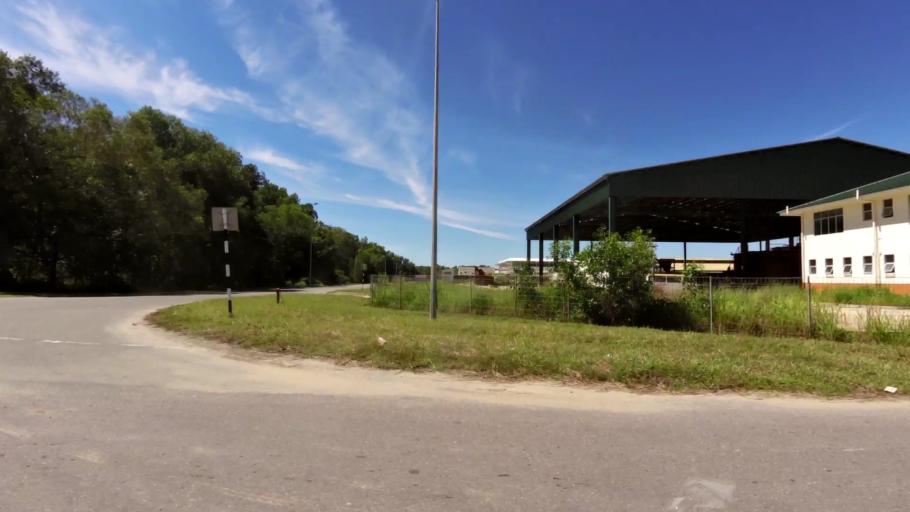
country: BN
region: Brunei and Muara
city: Bandar Seri Begawan
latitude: 5.0144
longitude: 115.0605
